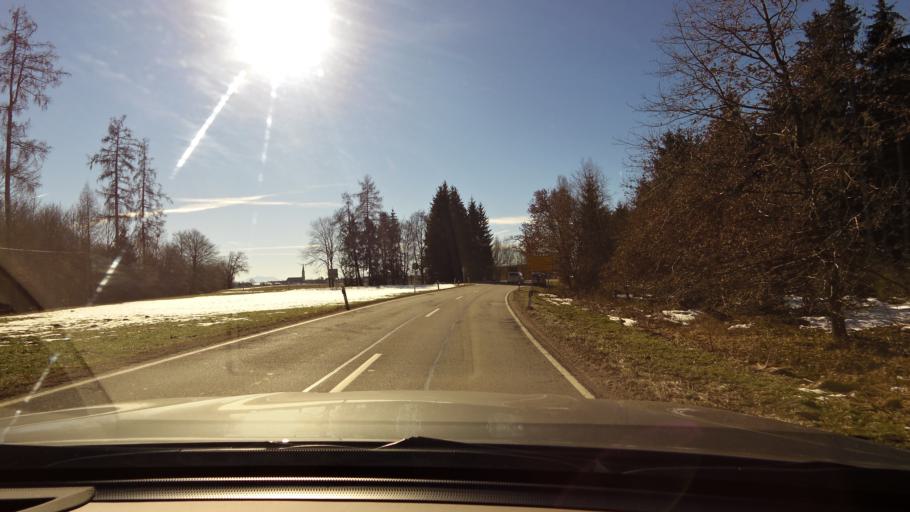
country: DE
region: Bavaria
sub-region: Upper Bavaria
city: Taufkirchen
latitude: 48.1571
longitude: 12.4566
